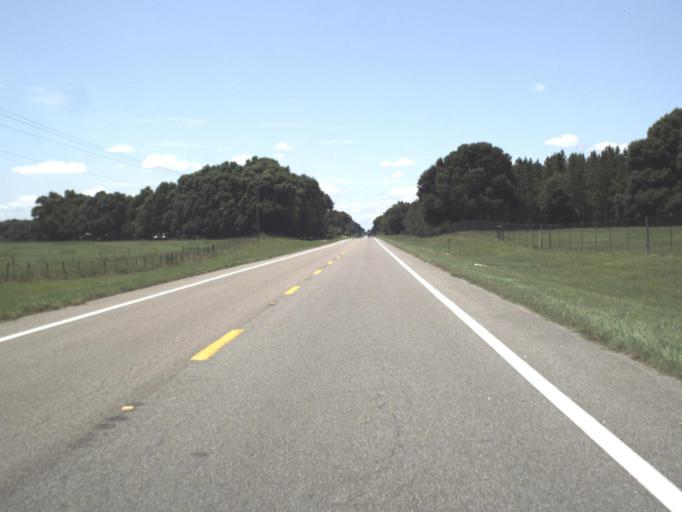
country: US
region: Florida
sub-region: Lafayette County
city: Mayo
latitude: 30.0228
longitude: -83.0496
